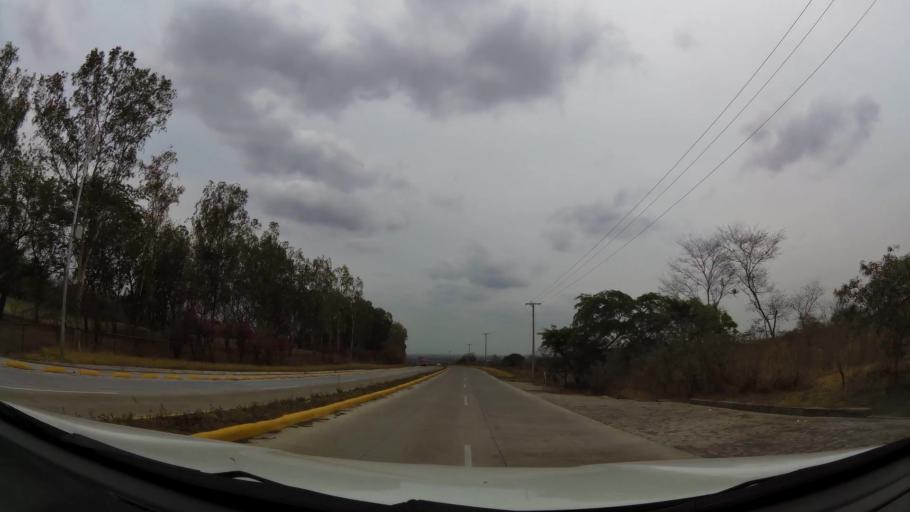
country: NI
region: Masaya
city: Ticuantepe
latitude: 12.0944
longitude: -86.1789
